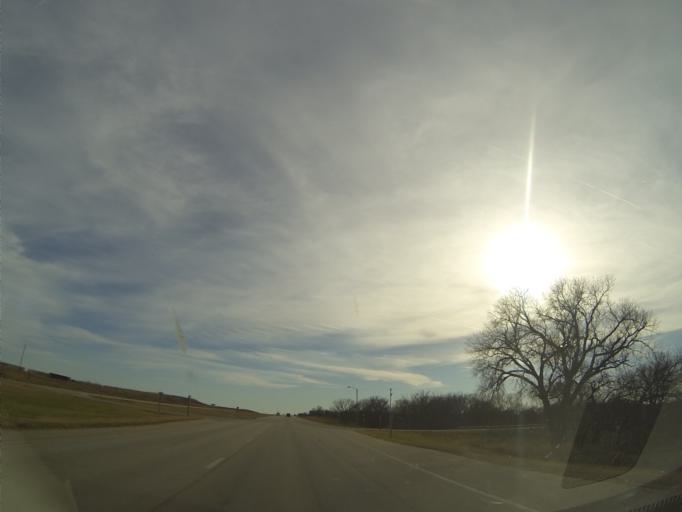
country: US
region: Kansas
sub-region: Ottawa County
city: Minneapolis
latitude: 39.1326
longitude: -97.6693
